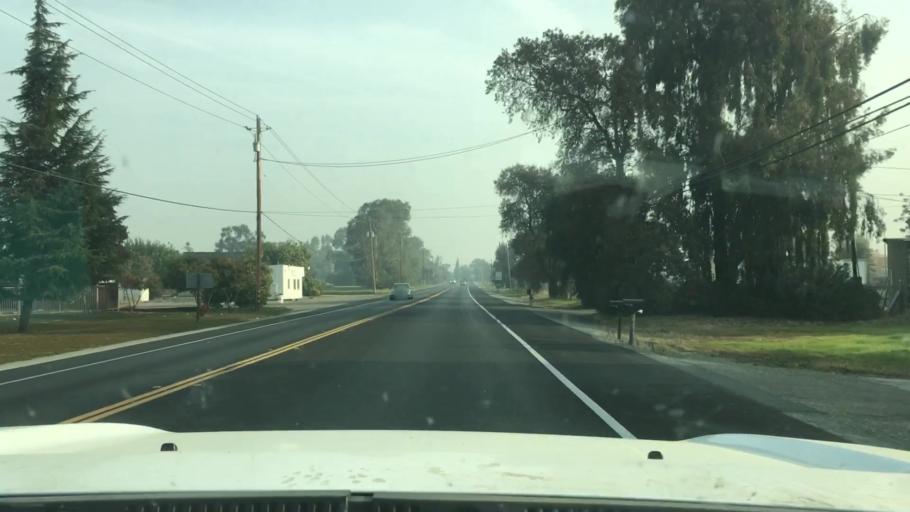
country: US
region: California
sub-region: San Joaquin County
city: Garden Acres
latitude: 37.9995
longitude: -121.2272
